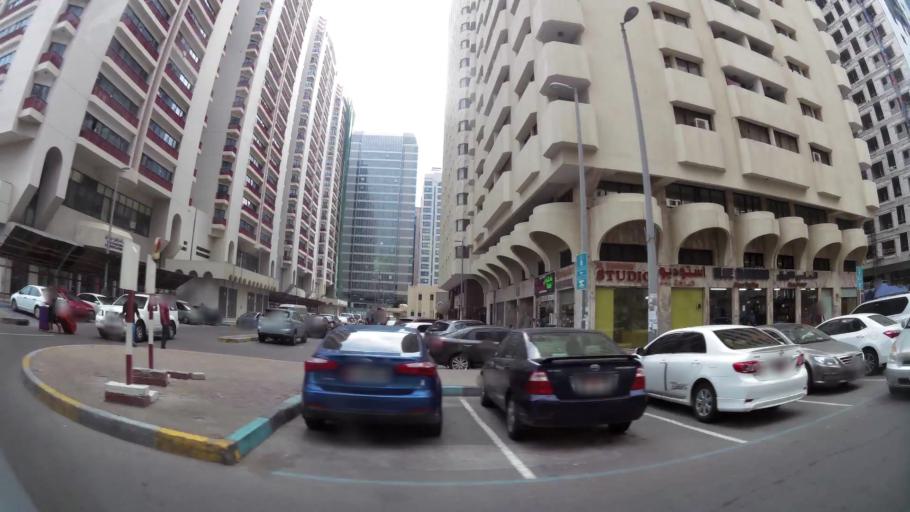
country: AE
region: Abu Dhabi
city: Abu Dhabi
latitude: 24.4944
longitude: 54.3796
